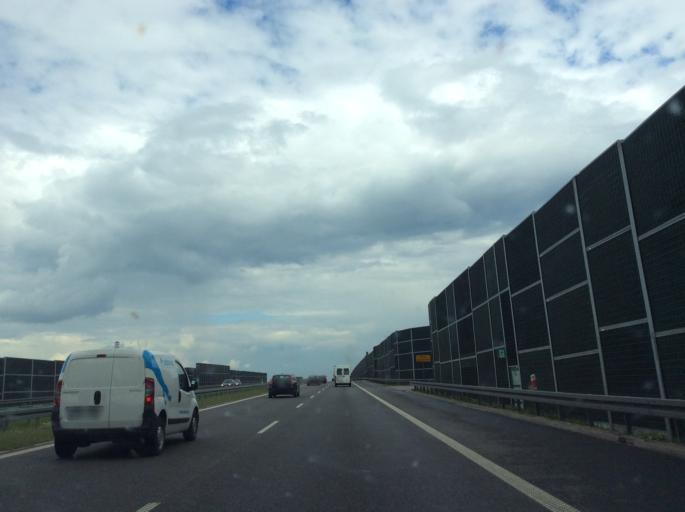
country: PL
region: Masovian Voivodeship
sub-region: Powiat pruszkowski
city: Brwinow
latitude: 52.1584
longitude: 20.7043
